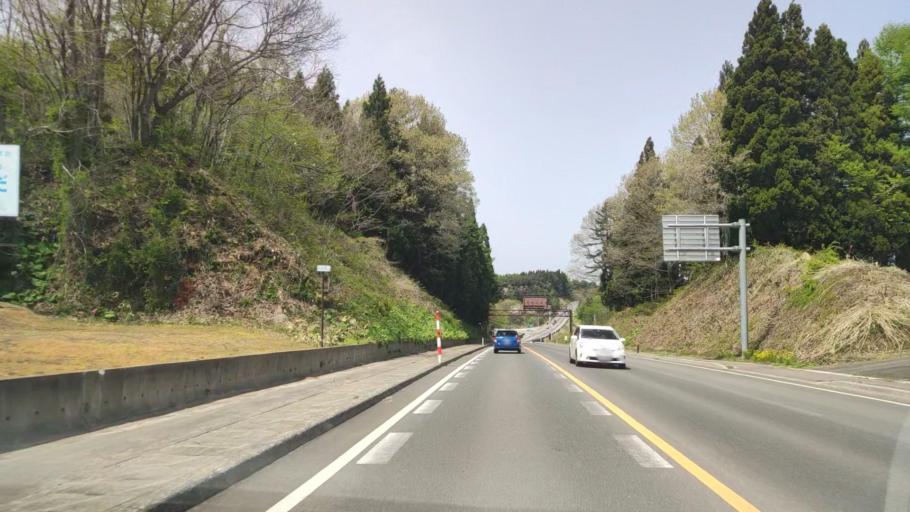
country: JP
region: Aomori
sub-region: Misawa Shi
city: Inuotose
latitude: 40.6608
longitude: 141.1900
